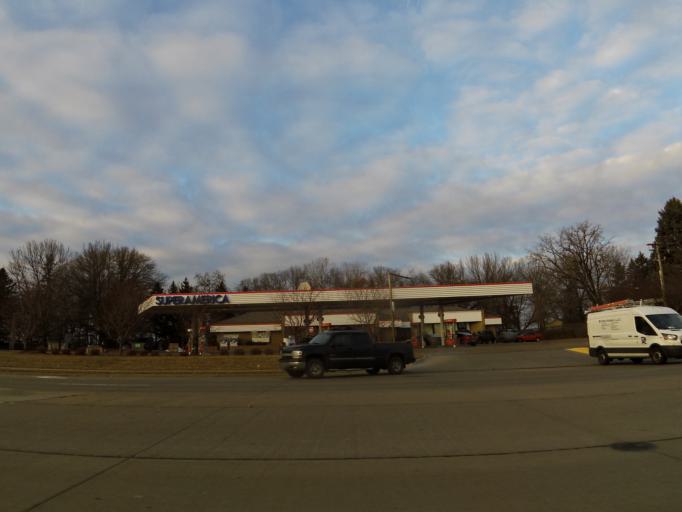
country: US
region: Minnesota
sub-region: Ramsey County
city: White Bear Lake
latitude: 45.0792
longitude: -93.0392
